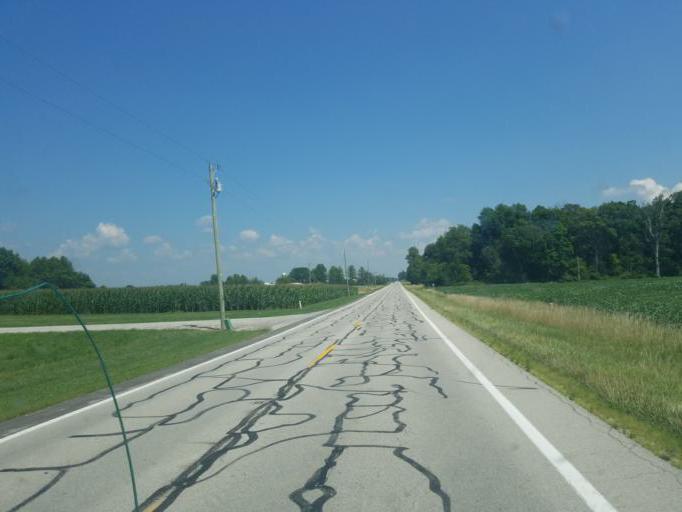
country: US
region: Ohio
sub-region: Shelby County
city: Jackson Center
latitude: 40.3959
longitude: -84.0757
